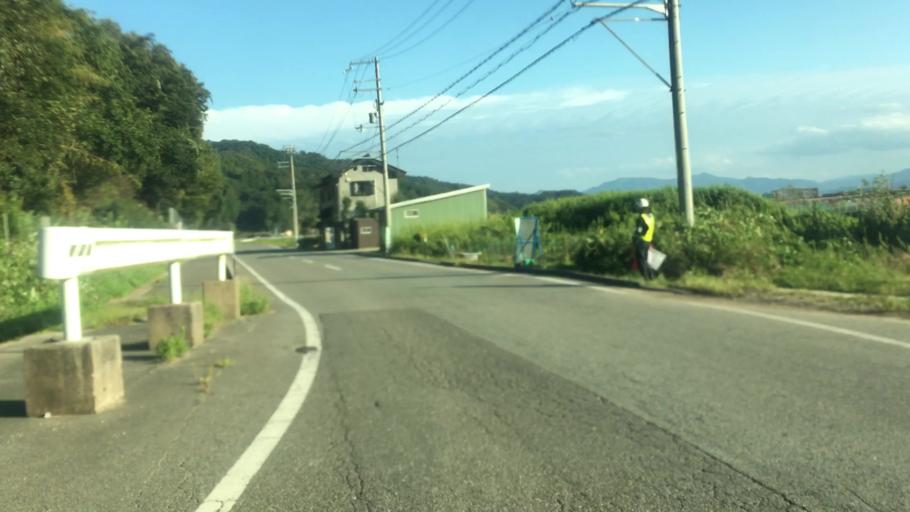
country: JP
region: Hyogo
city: Toyooka
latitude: 35.5866
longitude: 134.8055
